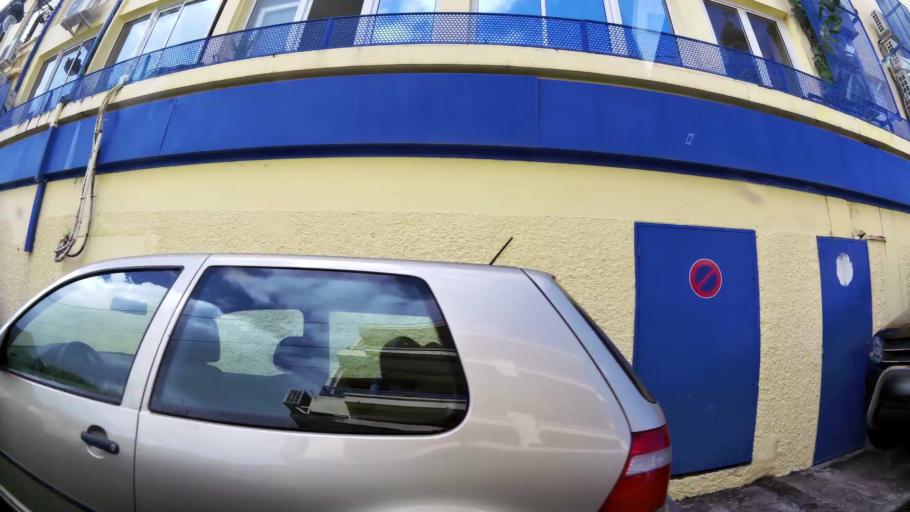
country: GP
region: Guadeloupe
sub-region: Guadeloupe
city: Basse-Terre
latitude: 15.9984
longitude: -61.7323
